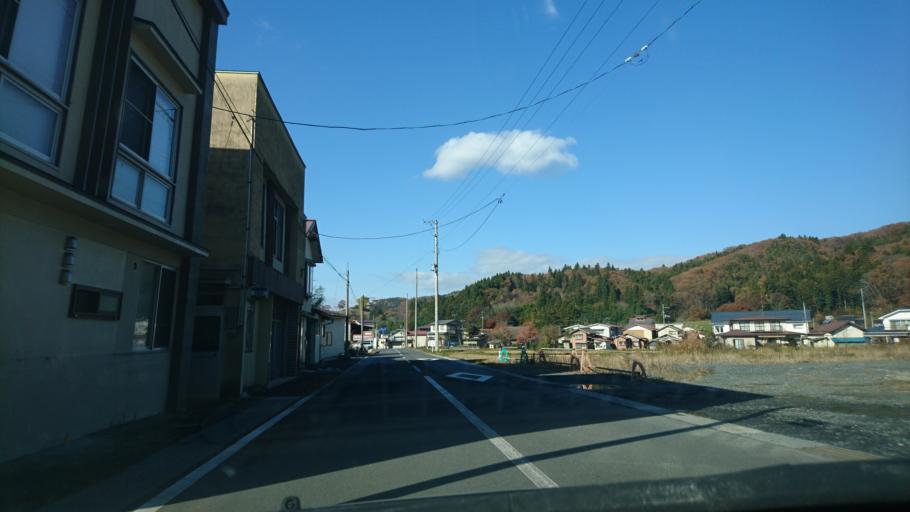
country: JP
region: Iwate
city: Ichinoseki
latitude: 39.0165
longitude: 141.4059
